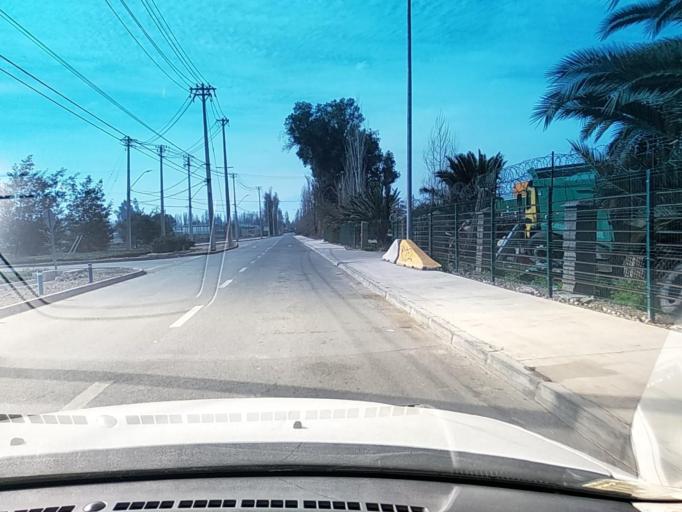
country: CL
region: Santiago Metropolitan
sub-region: Provincia de Chacabuco
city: Chicureo Abajo
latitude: -33.2868
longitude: -70.7327
